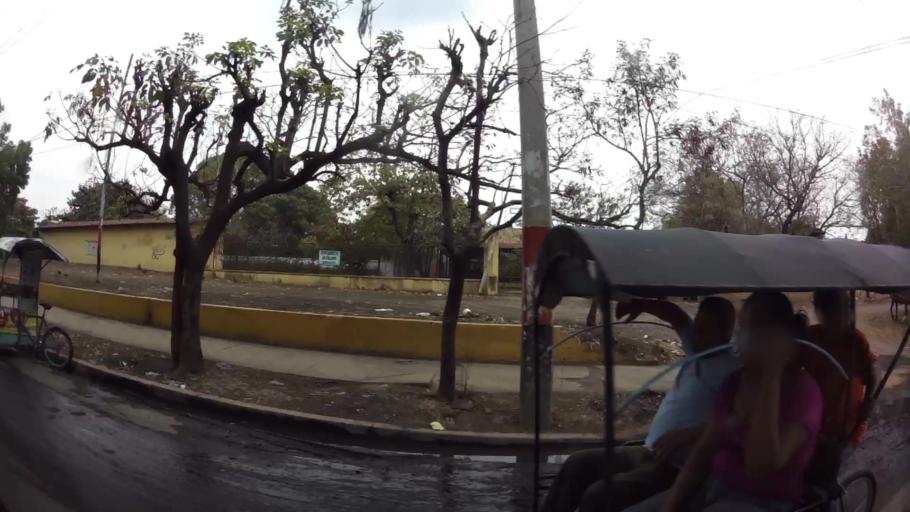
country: NI
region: Leon
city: Leon
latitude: 12.4442
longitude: -86.8729
